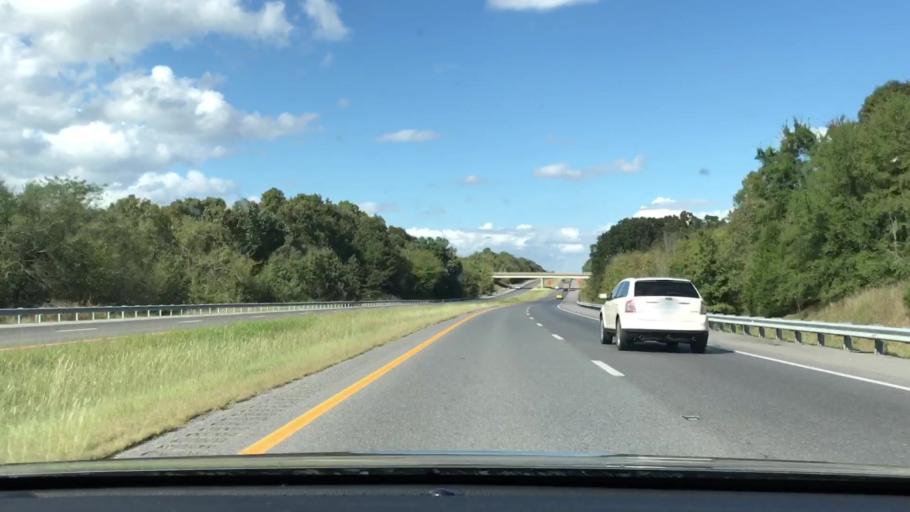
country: US
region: Kentucky
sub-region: Marshall County
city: Calvert City
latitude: 36.9522
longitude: -88.3500
